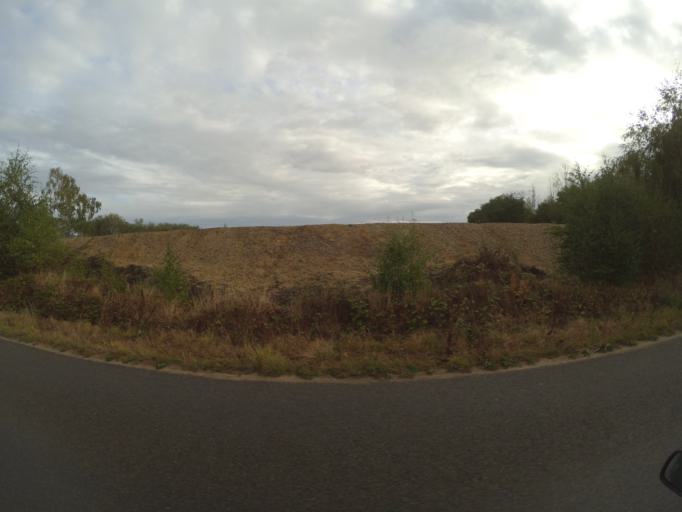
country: FR
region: Pays de la Loire
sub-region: Departement de la Loire-Atlantique
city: La Planche
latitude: 47.0246
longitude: -1.4536
